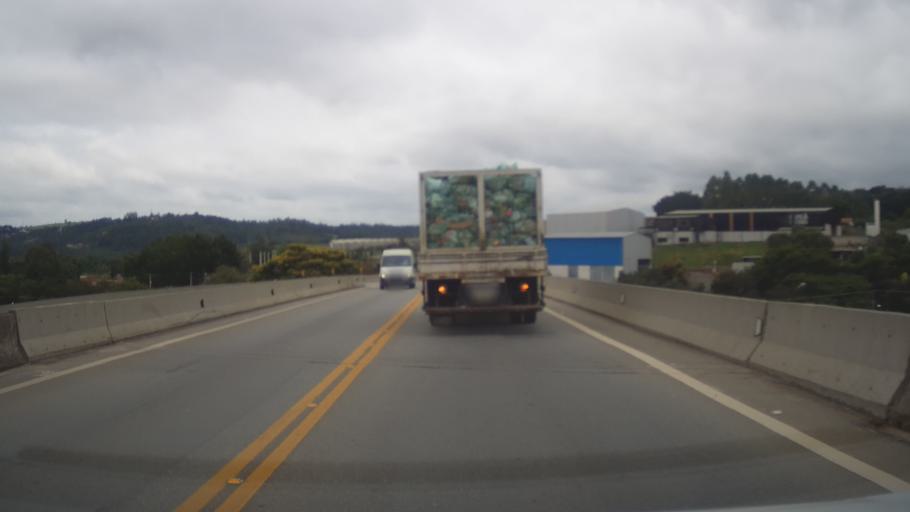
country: BR
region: Sao Paulo
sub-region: Louveira
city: Louveira
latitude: -23.0861
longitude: -46.9759
